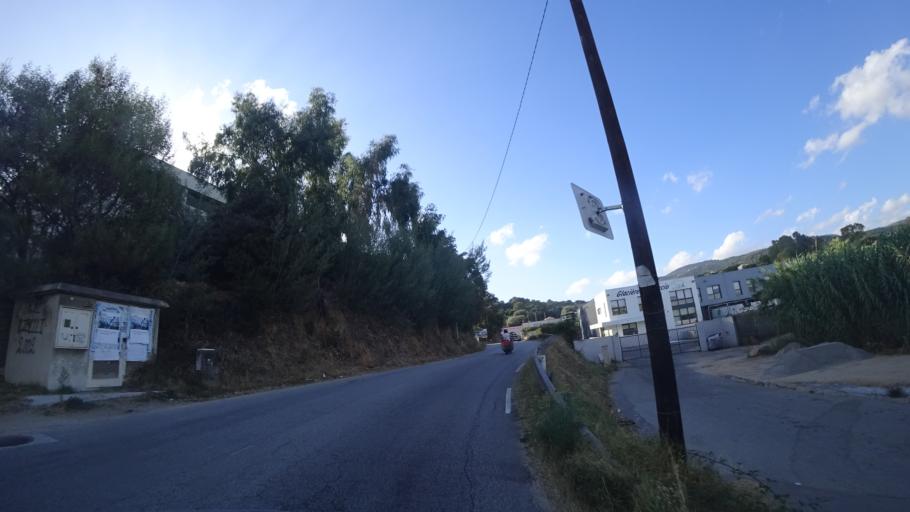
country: FR
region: Corsica
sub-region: Departement de la Corse-du-Sud
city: Ajaccio
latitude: 41.9412
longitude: 8.7361
